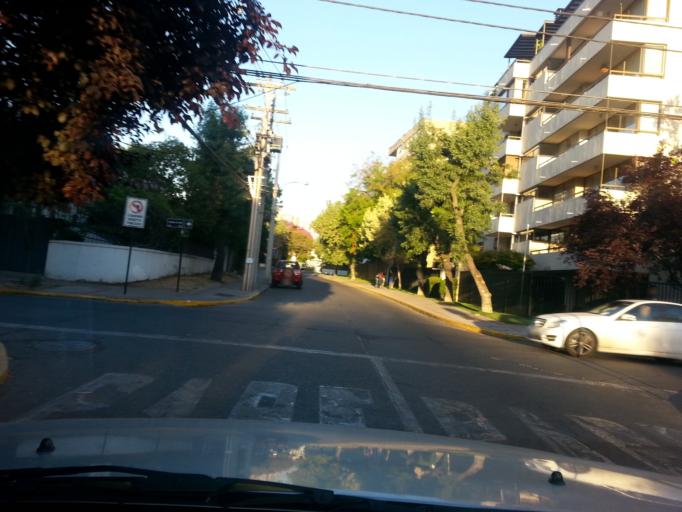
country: CL
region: Santiago Metropolitan
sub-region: Provincia de Santiago
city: Villa Presidente Frei, Nunoa, Santiago, Chile
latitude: -33.4301
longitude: -70.5919
